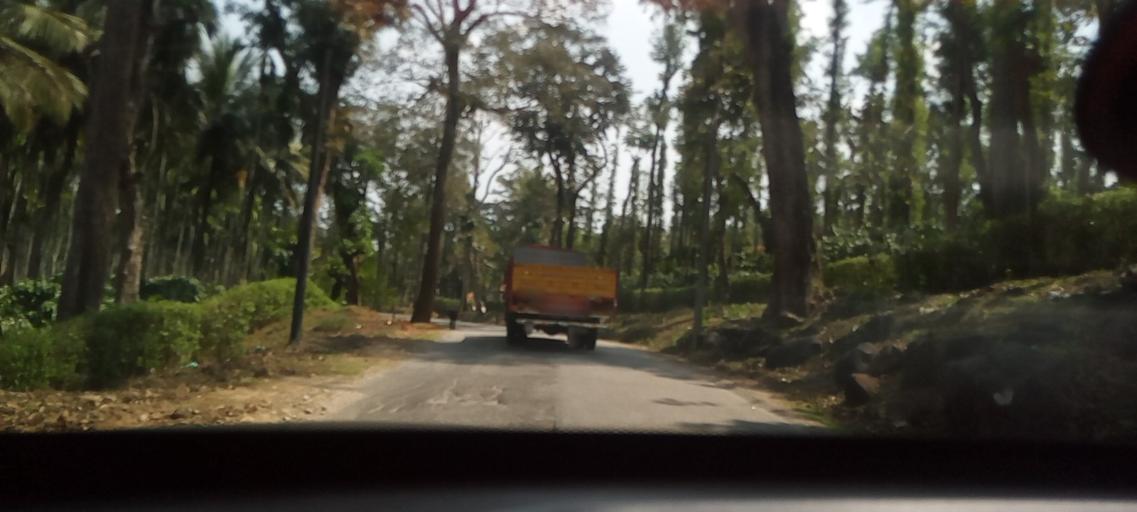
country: IN
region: Karnataka
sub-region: Chikmagalur
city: Mudigere
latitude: 13.3250
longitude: 75.5618
